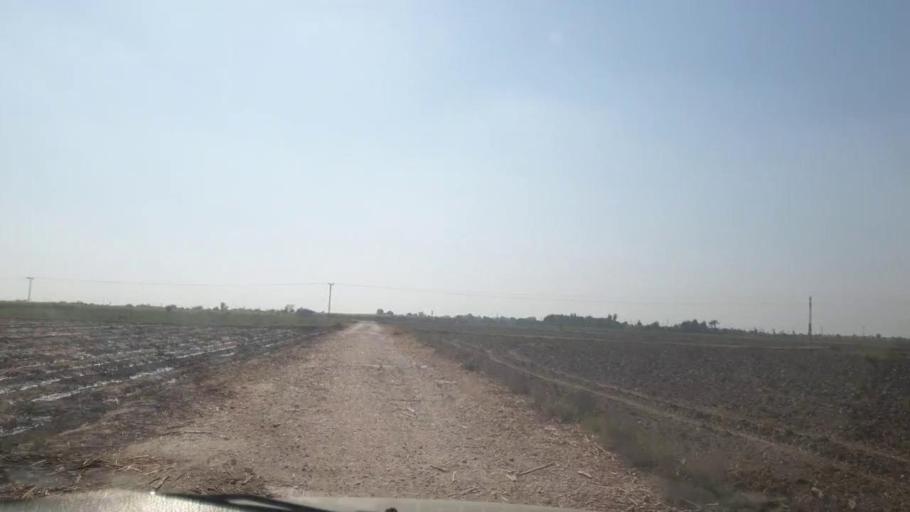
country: PK
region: Sindh
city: Mirpur Khas
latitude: 25.4765
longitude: 69.1295
